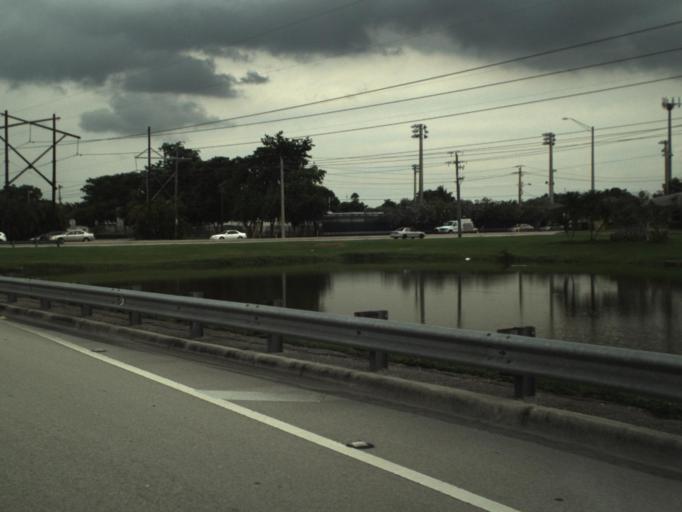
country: US
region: Florida
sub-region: Broward County
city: Cooper City
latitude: 26.0305
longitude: -80.2656
